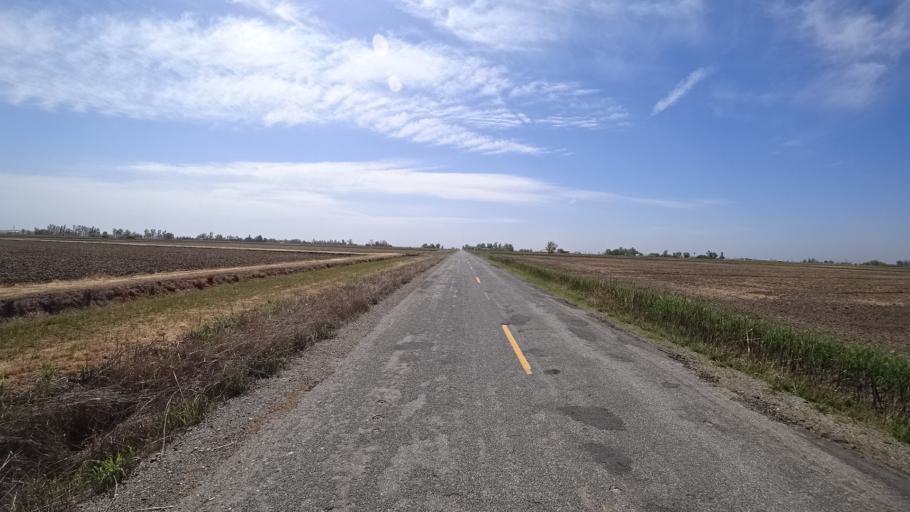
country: US
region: California
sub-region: Glenn County
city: Hamilton City
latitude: 39.5915
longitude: -122.0463
